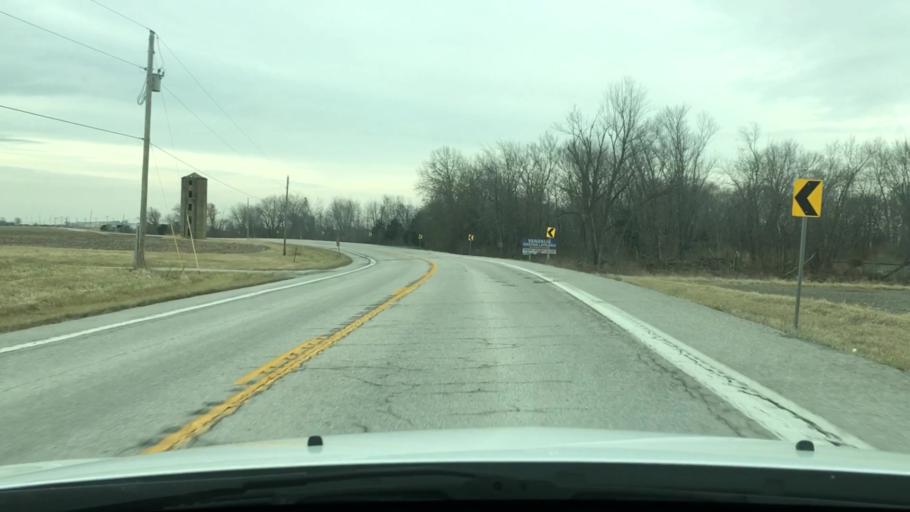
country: US
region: Missouri
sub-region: Audrain County
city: Vandalia
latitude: 39.2789
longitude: -91.5619
